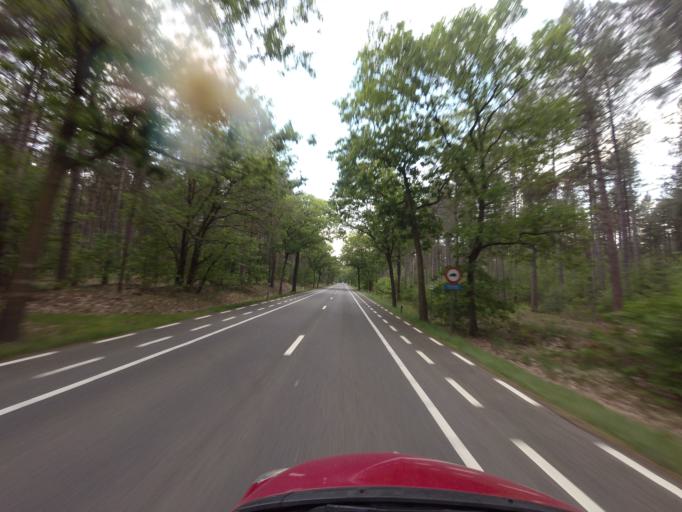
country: BE
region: Flanders
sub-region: Provincie Limburg
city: Overpelt
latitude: 51.1809
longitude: 5.3637
